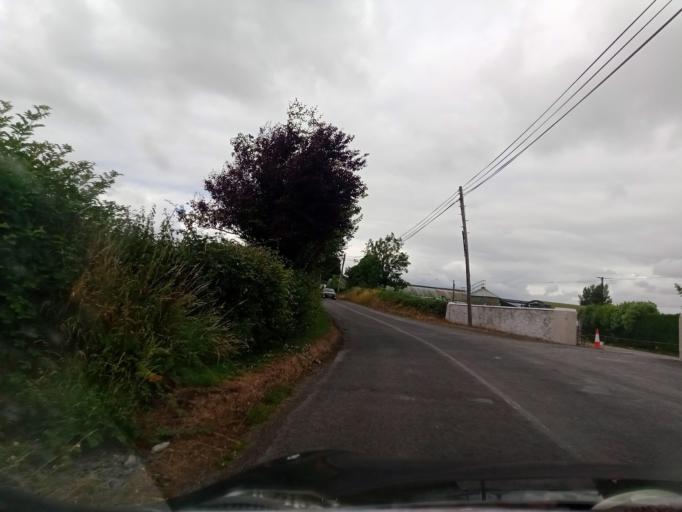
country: IE
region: Leinster
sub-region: Laois
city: Stradbally
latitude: 52.9743
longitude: -7.1792
